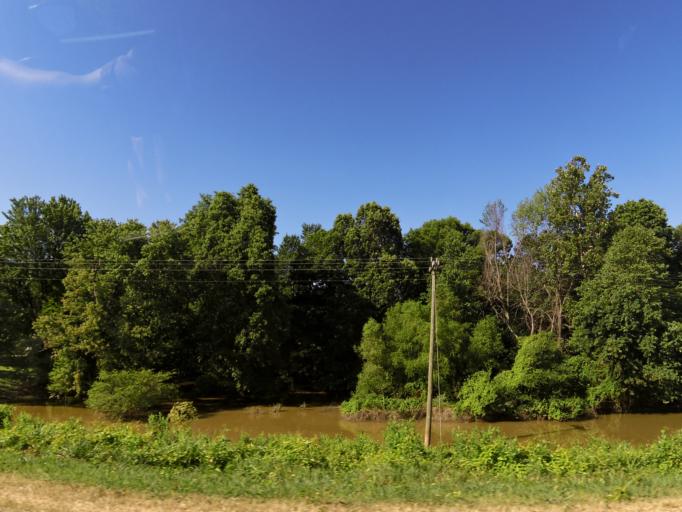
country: US
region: Arkansas
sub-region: Clay County
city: Corning
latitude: 36.4033
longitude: -90.5437
